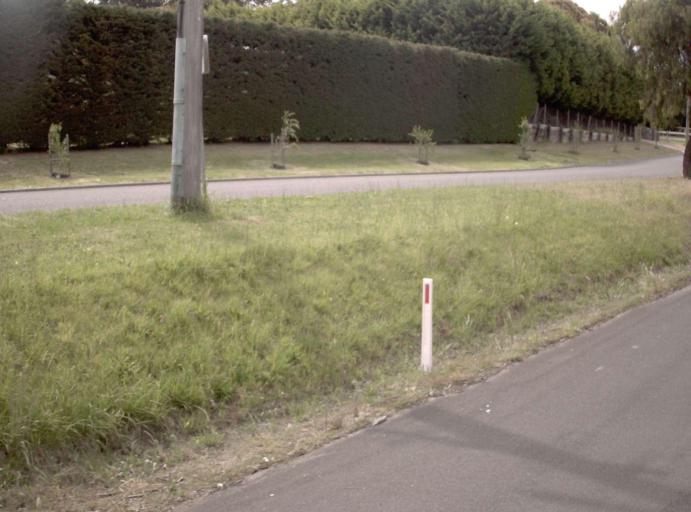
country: AU
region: Victoria
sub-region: Mornington Peninsula
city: Baxter
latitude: -38.1871
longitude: 145.1411
